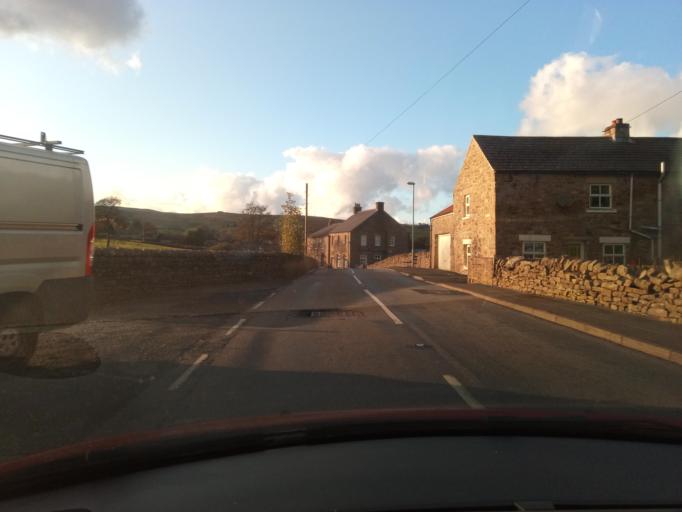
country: GB
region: England
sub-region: County Durham
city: Newbiggin
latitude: 54.7476
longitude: -2.2164
